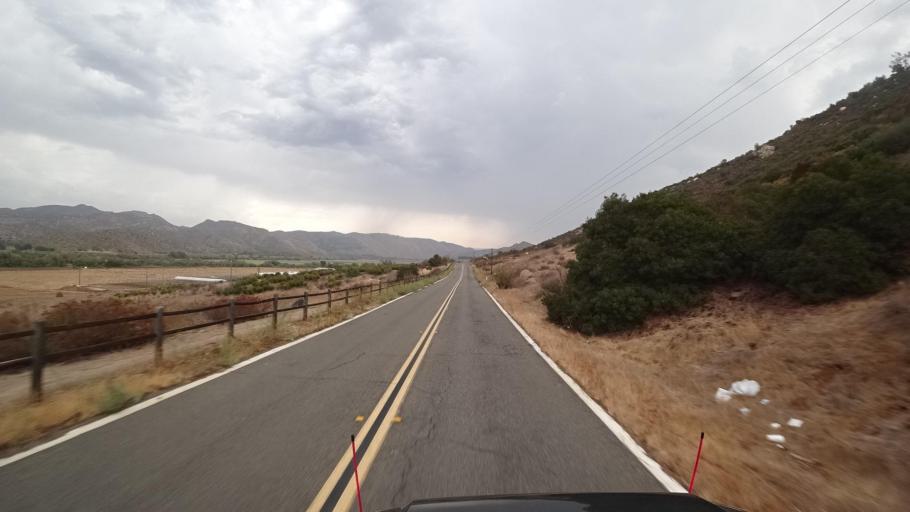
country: US
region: California
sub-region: San Diego County
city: San Pasqual
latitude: 33.0755
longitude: -116.9957
